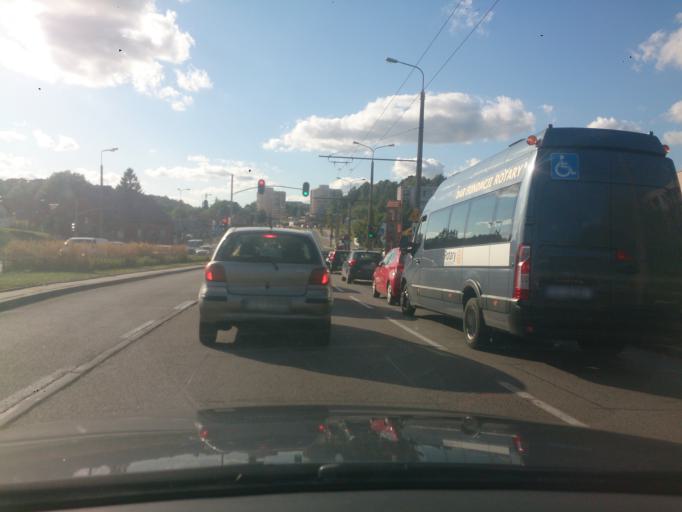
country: PL
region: Pomeranian Voivodeship
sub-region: Gdynia
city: Wielki Kack
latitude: 54.4699
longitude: 18.4978
